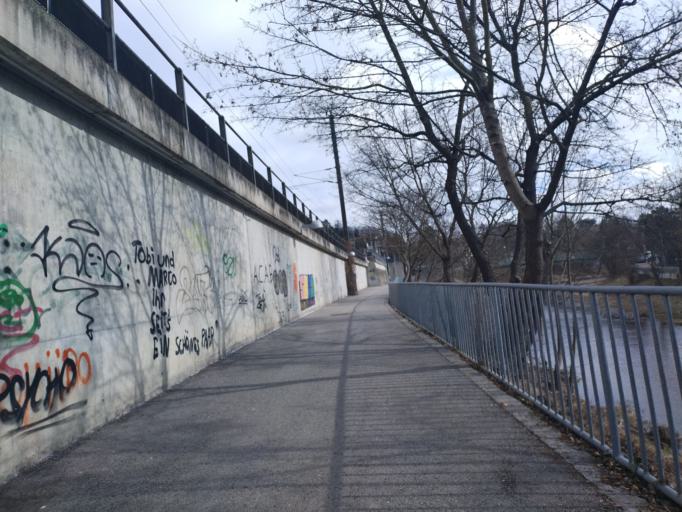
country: AT
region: Lower Austria
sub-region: Politischer Bezirk Wien-Umgebung
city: Purkersdorf
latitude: 48.2100
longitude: 16.2105
